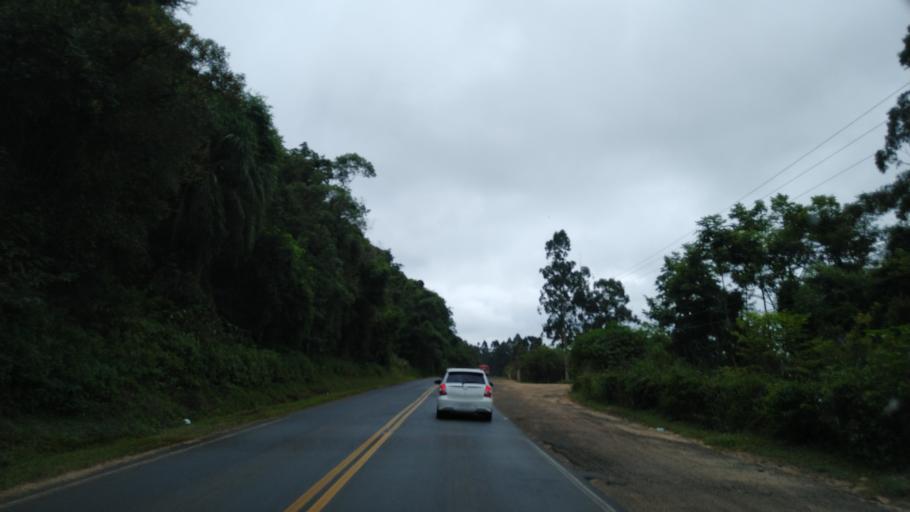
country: BR
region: Parana
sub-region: Uniao Da Vitoria
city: Uniao da Vitoria
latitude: -26.2270
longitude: -51.1271
